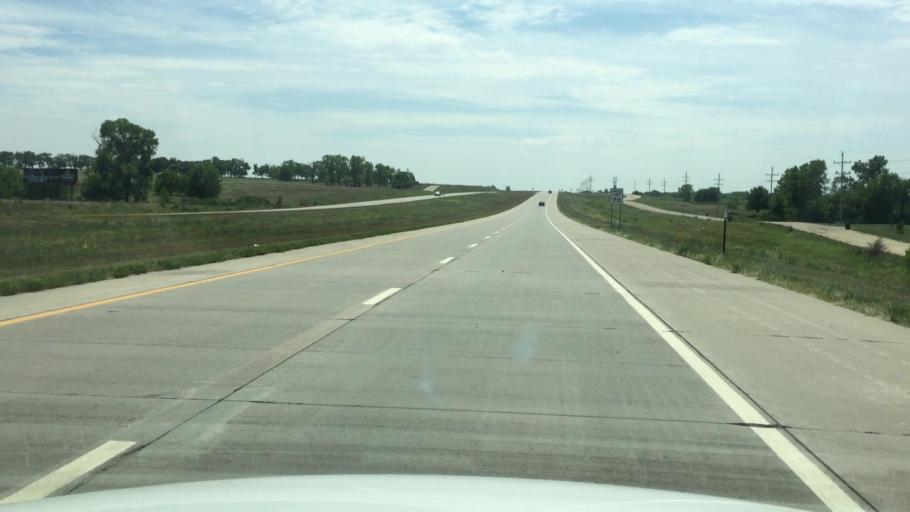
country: US
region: Kansas
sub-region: Shawnee County
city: Silver Lake
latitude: 39.2440
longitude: -95.7197
